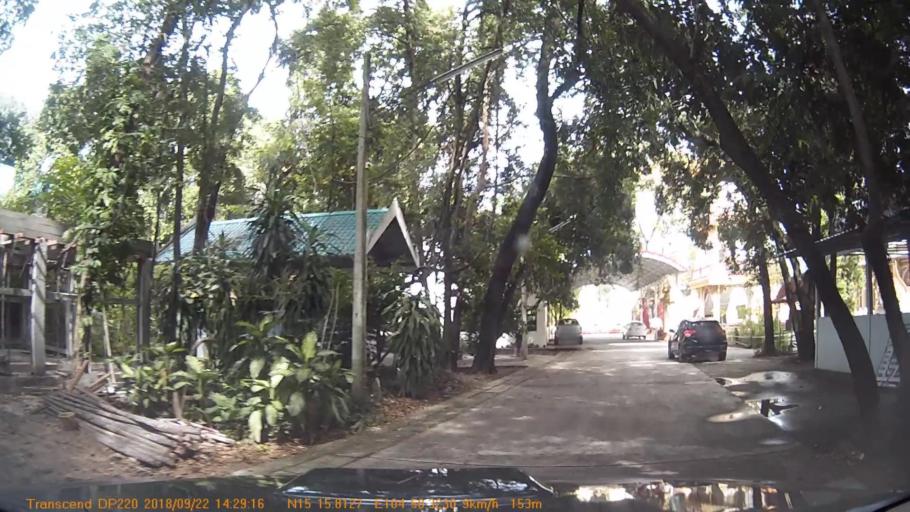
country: TH
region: Changwat Ubon Ratchathani
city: Ubon Ratchathani
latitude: 15.2636
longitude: 104.8388
